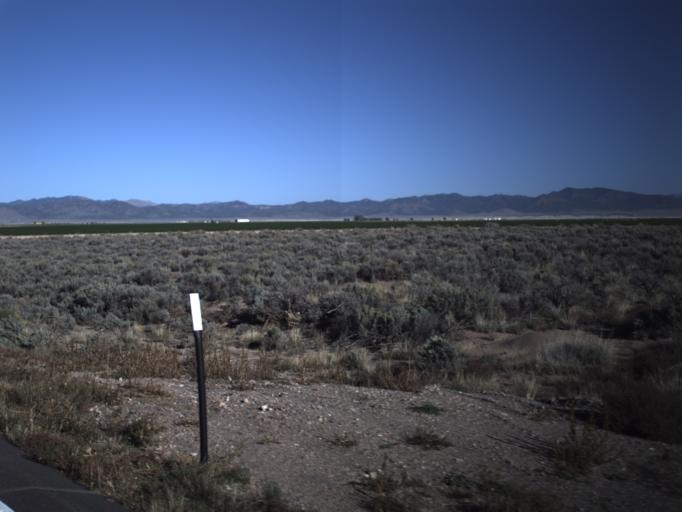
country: US
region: Utah
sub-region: Washington County
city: Enterprise
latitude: 37.7500
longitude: -113.7695
